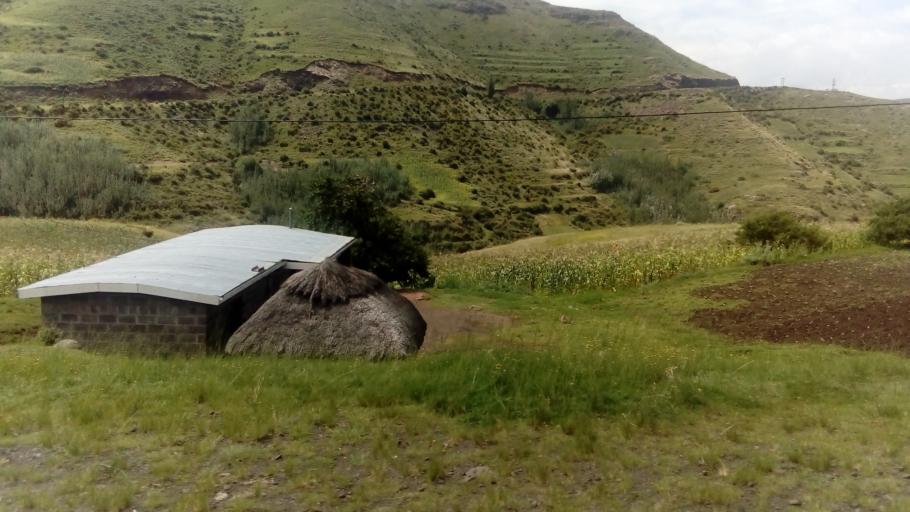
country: LS
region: Thaba-Tseka
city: Thaba-Tseka
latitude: -29.1446
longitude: 28.4904
